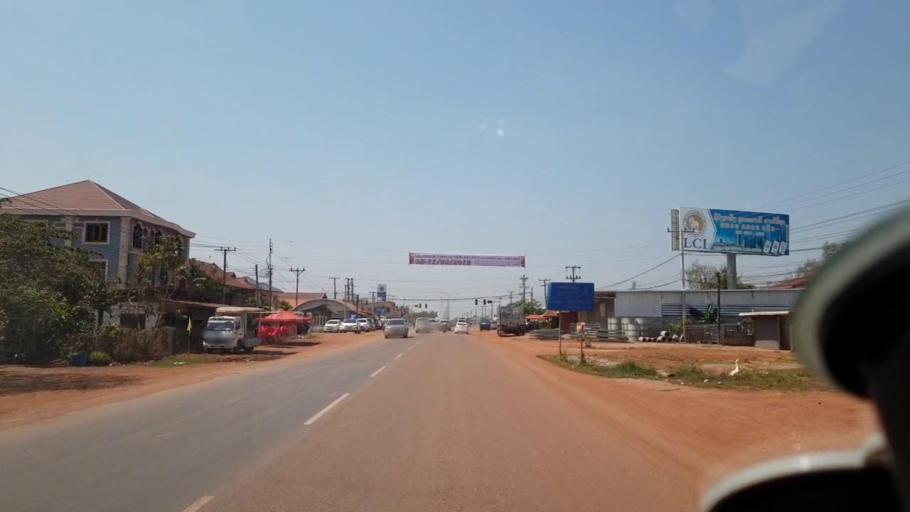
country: LA
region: Vientiane
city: Vientiane
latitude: 18.0738
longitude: 102.7482
